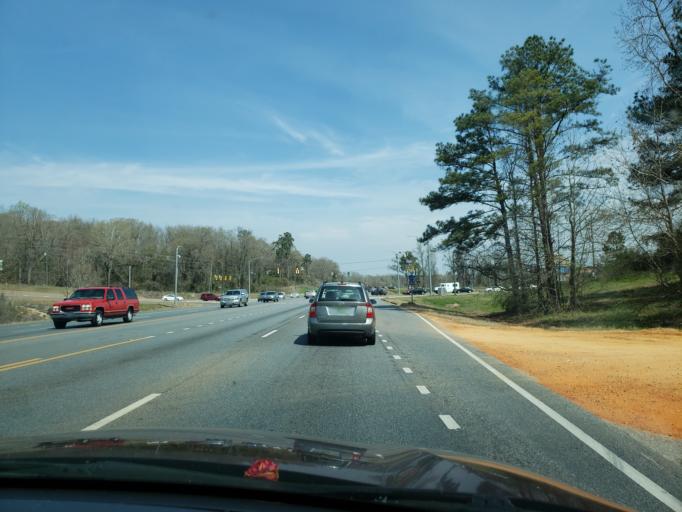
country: US
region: Alabama
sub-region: Elmore County
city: Millbrook
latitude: 32.4947
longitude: -86.4029
